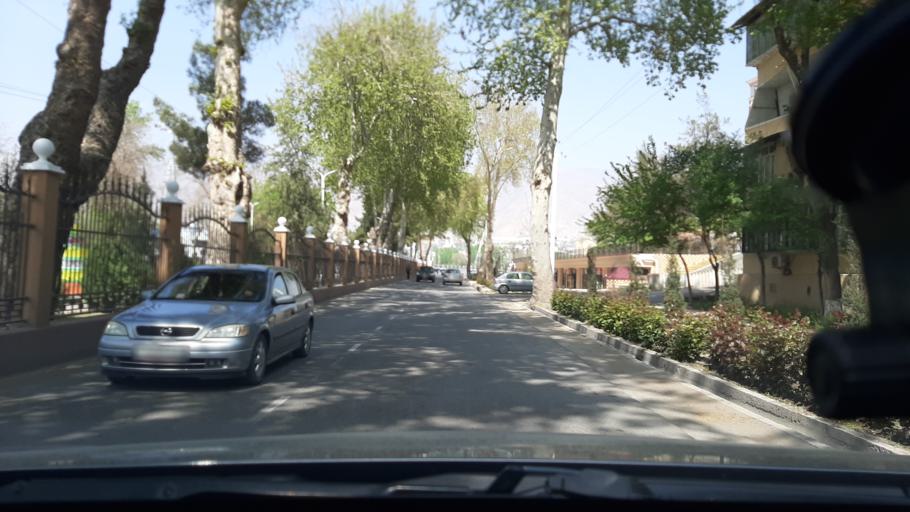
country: TJ
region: Viloyati Sughd
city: Khujand
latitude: 40.2866
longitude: 69.6187
